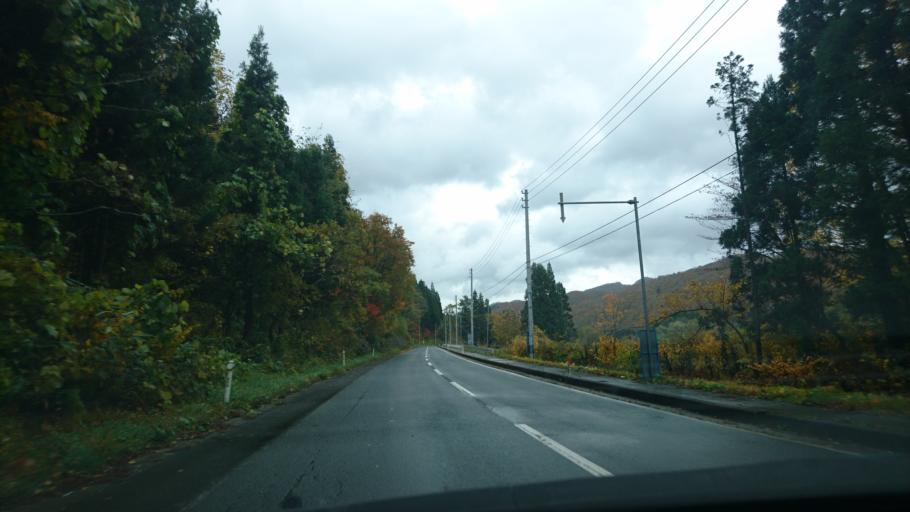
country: JP
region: Iwate
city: Shizukuishi
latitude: 39.5020
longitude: 140.8189
